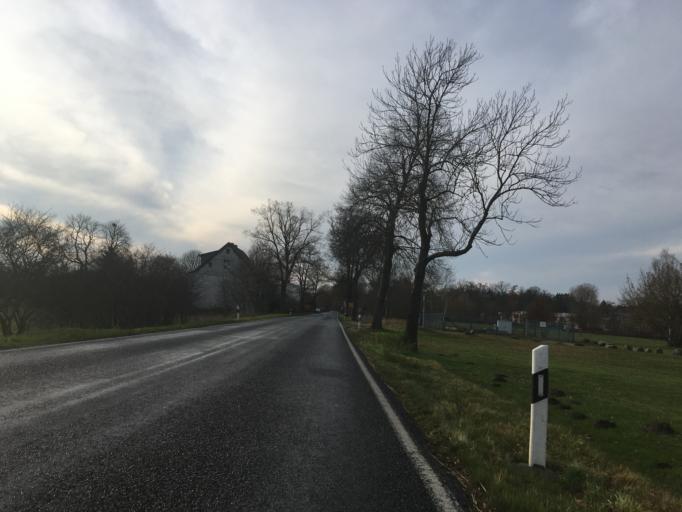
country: DE
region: Brandenburg
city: Eberswalde
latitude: 52.8436
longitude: 13.8326
